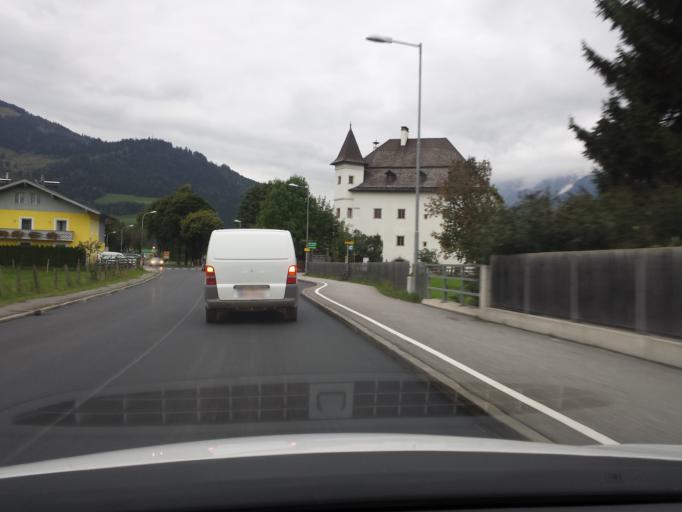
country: AT
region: Salzburg
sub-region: Politischer Bezirk Zell am See
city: Saalfelden am Steinernen Meer
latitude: 47.4309
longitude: 12.8369
